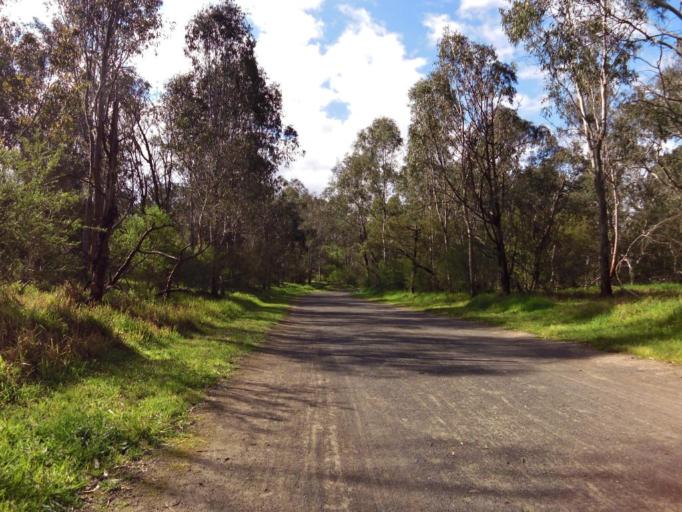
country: AU
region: Victoria
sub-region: Banyule
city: Viewbank
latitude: -37.7499
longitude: 145.0949
